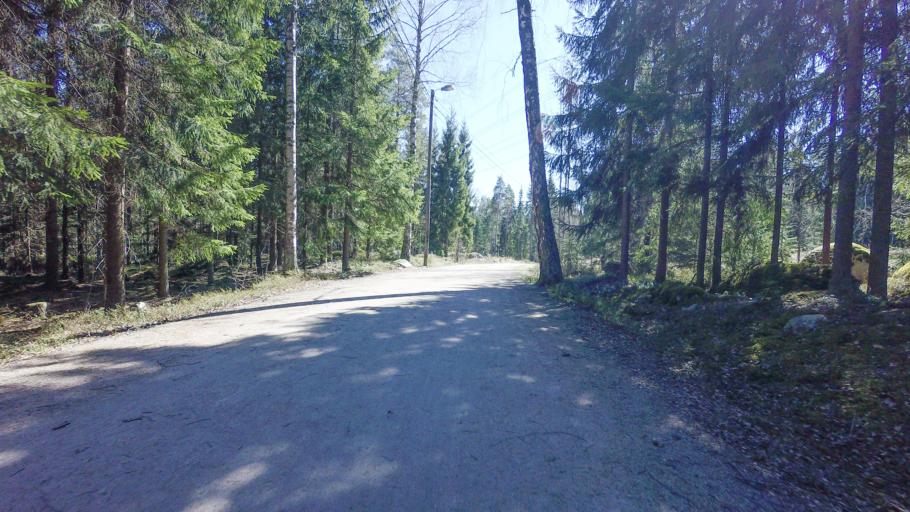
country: FI
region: Uusimaa
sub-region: Helsinki
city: Vantaa
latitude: 60.2297
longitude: 25.1459
